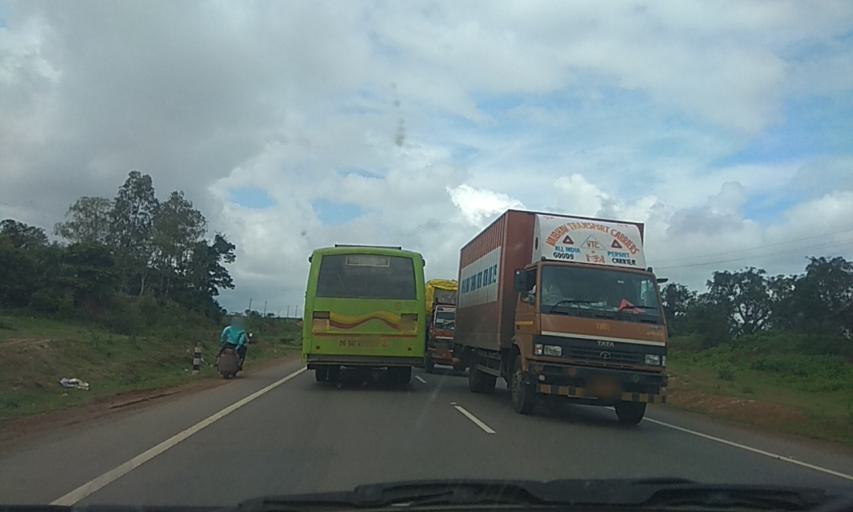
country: IN
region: Karnataka
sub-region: Dharwad
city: Hubli
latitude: 15.4004
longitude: 74.9992
